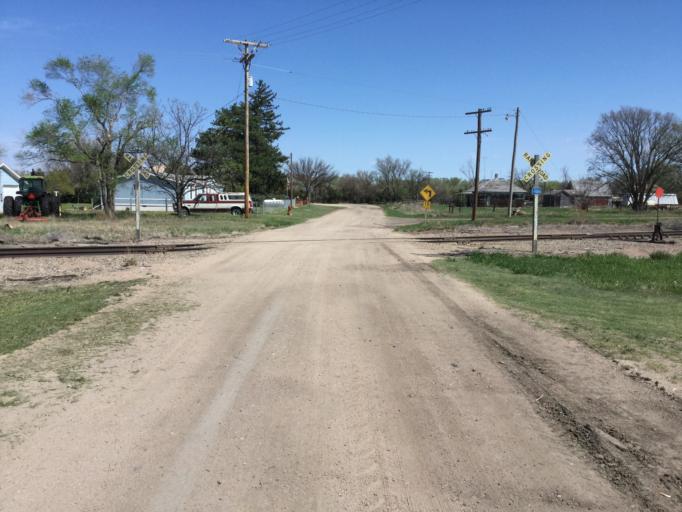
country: US
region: Kansas
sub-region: Decatur County
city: Oberlin
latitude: 39.6821
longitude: -100.2956
